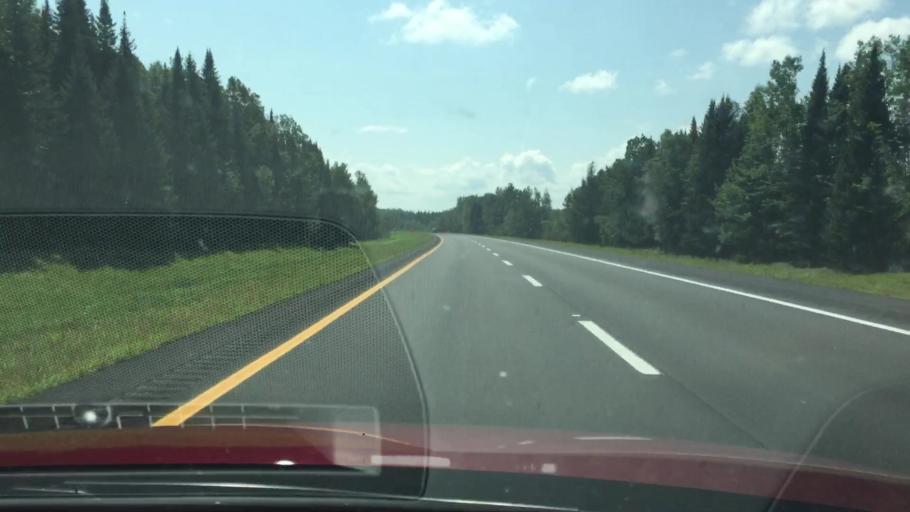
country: US
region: Maine
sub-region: Penobscot County
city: Patten
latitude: 45.8902
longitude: -68.4042
